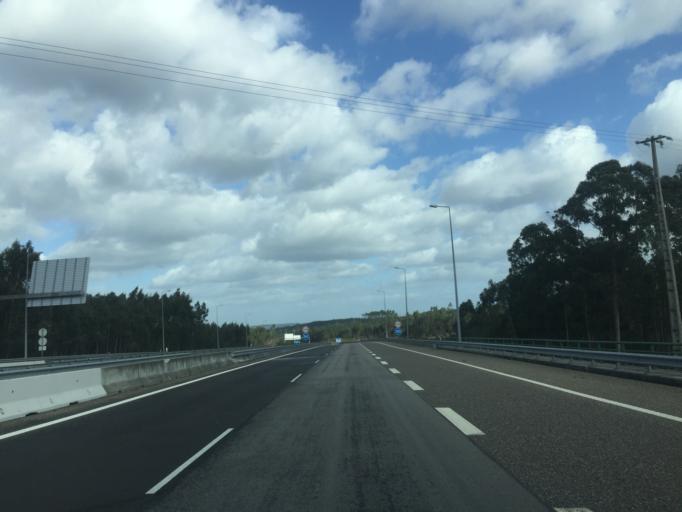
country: PT
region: Leiria
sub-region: Marinha Grande
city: Marinha Grande
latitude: 39.7460
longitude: -8.8811
